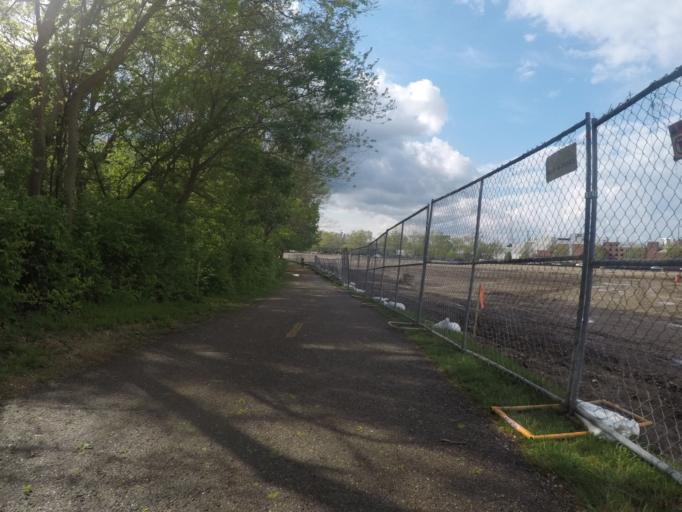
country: US
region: Ohio
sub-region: Franklin County
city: Grandview Heights
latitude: 39.9863
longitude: -83.0210
